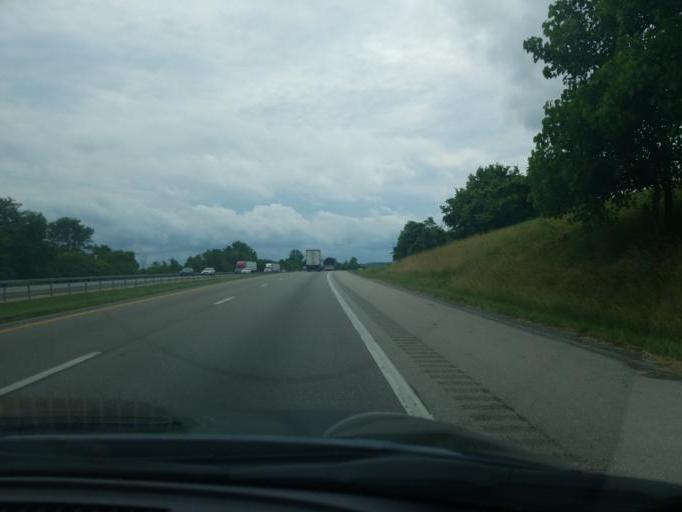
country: US
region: Indiana
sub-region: Switzerland County
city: Vevay
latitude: 38.6670
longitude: -85.0229
